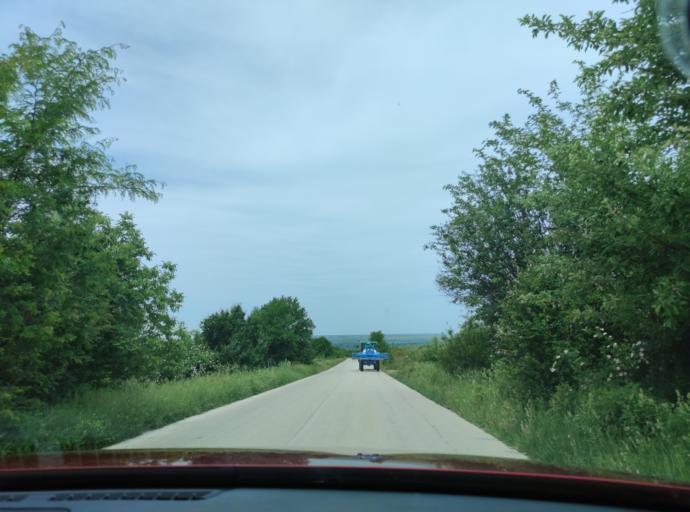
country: BG
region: Pleven
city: Iskur
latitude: 43.5302
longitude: 24.3065
